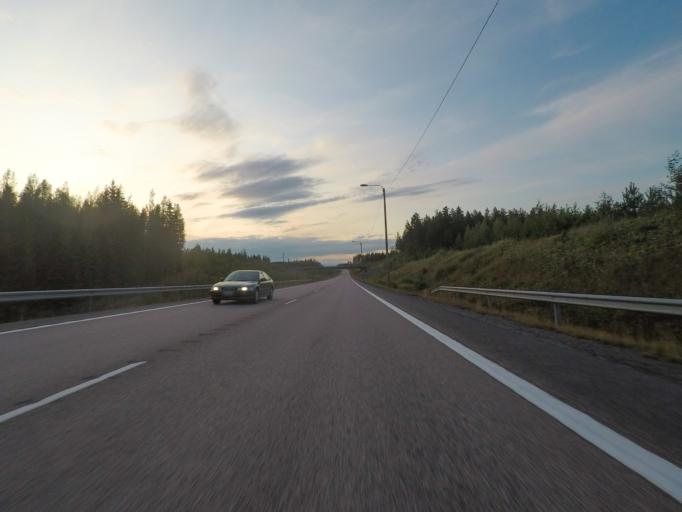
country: FI
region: Central Finland
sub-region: Jyvaeskylae
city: Toivakka
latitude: 62.1037
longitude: 25.9820
